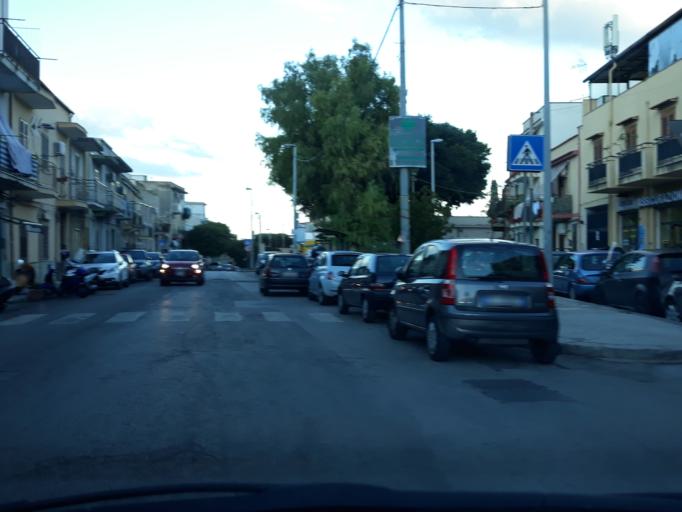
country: IT
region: Sicily
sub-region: Palermo
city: Villa Ciambra
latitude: 38.0902
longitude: 13.3310
